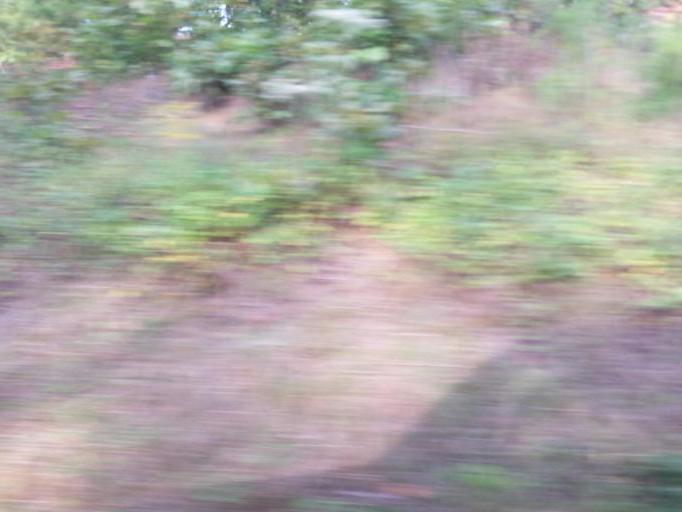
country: US
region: Tennessee
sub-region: Blount County
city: Wildwood
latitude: 35.8471
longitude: -83.8712
